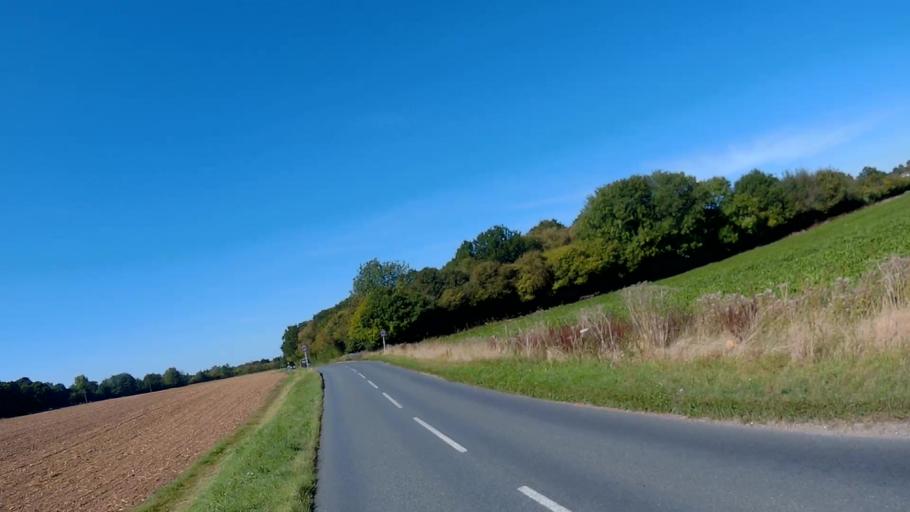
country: GB
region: England
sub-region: Hampshire
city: Basingstoke
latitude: 51.2541
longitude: -1.1636
